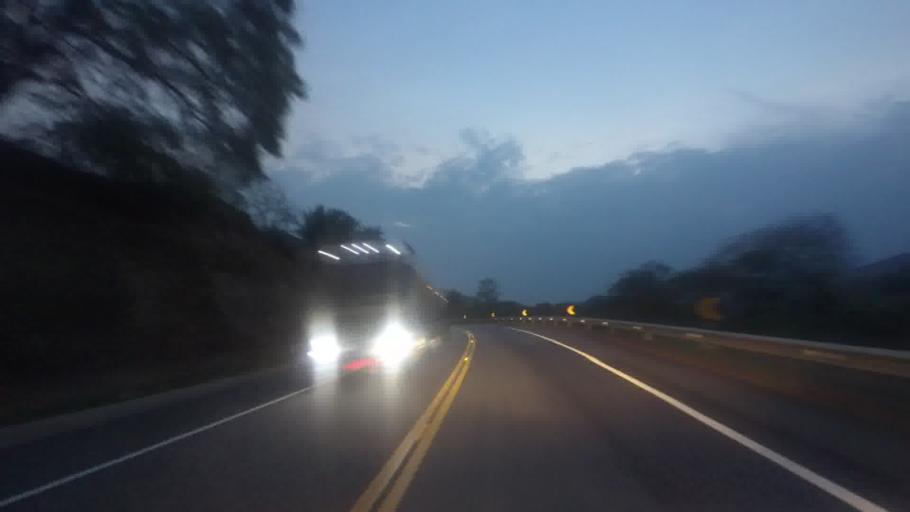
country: BR
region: Minas Gerais
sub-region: Alem Paraiba
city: Alem Paraiba
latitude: -21.9382
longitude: -42.8079
